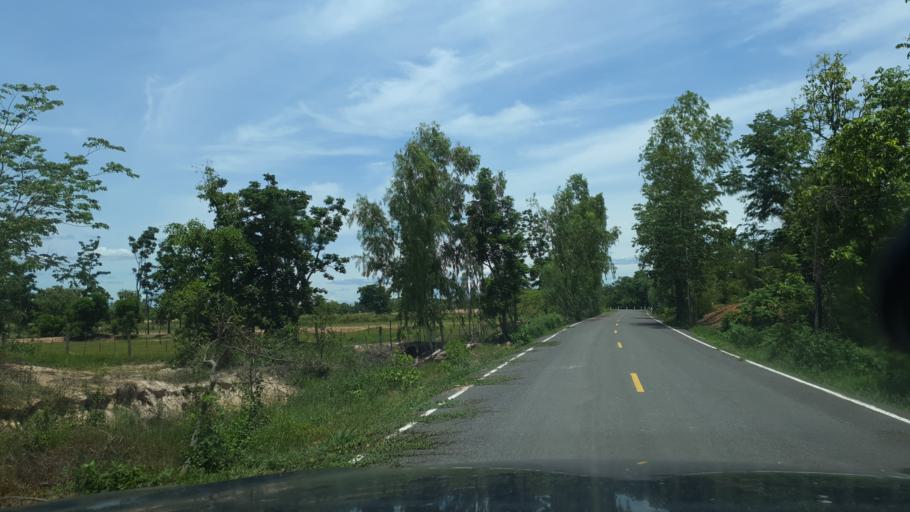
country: TH
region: Sukhothai
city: Ban Na
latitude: 17.1505
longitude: 99.6576
